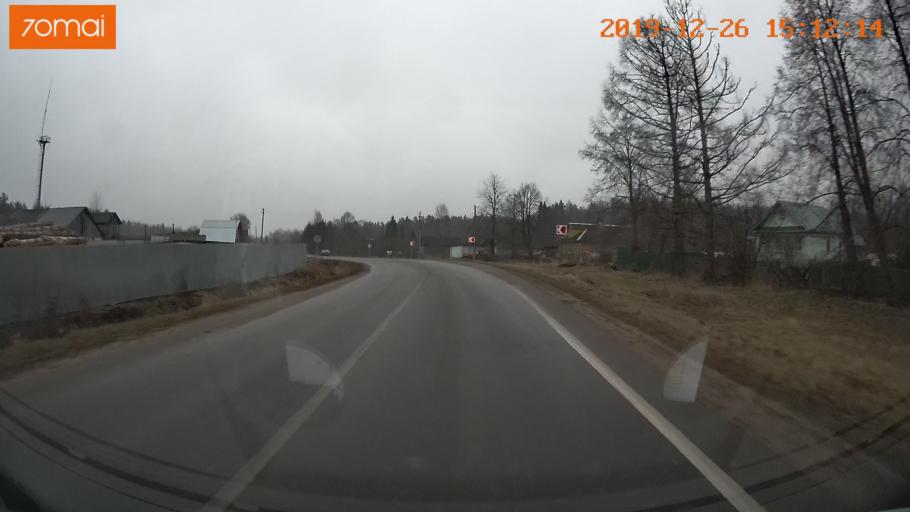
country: RU
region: Jaroslavl
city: Rybinsk
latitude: 58.1288
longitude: 38.8725
